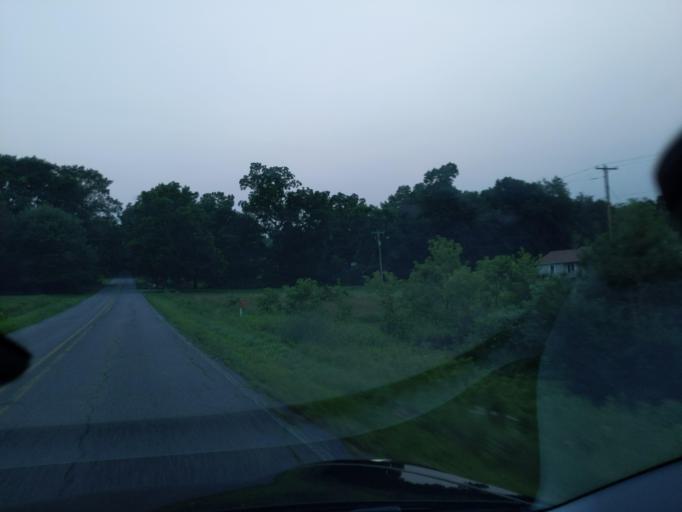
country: US
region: Michigan
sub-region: Ingham County
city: Leslie
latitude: 42.3715
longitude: -84.5158
